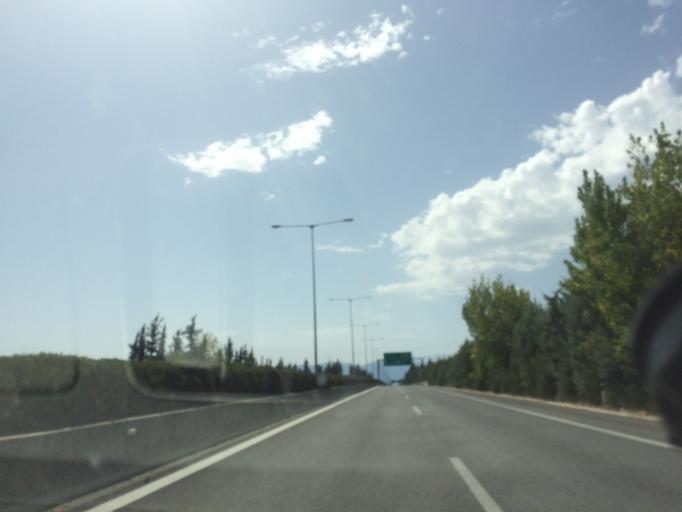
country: GR
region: Central Greece
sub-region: Nomos Fthiotidos
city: Pelasgia
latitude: 38.9586
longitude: 22.8807
